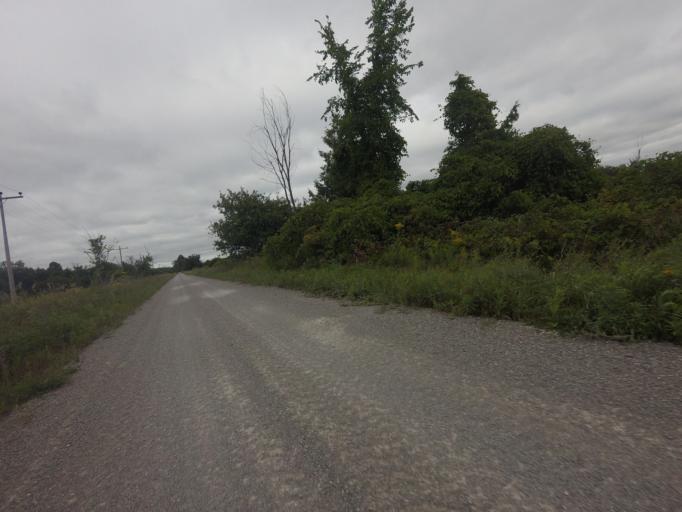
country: CA
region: Ontario
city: Omemee
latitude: 44.4594
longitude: -78.7593
